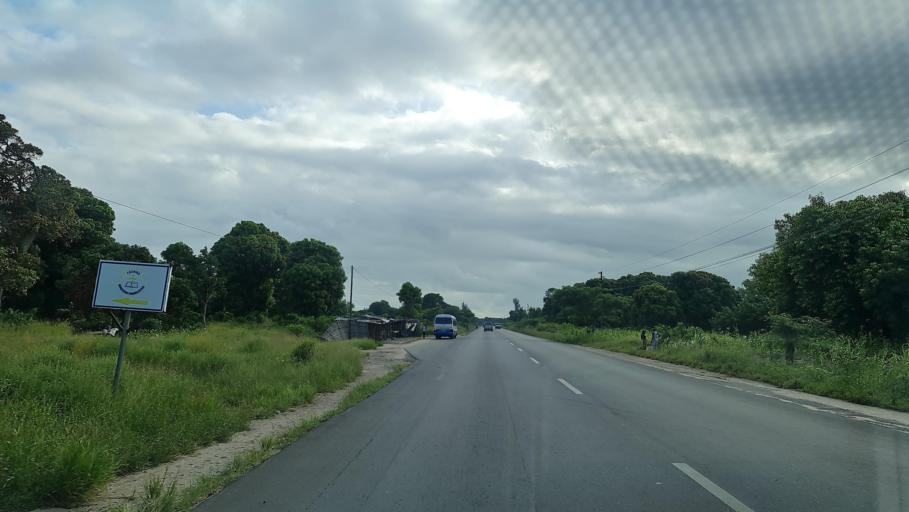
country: MZ
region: Maputo
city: Manhica
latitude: -25.4153
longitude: 32.7369
